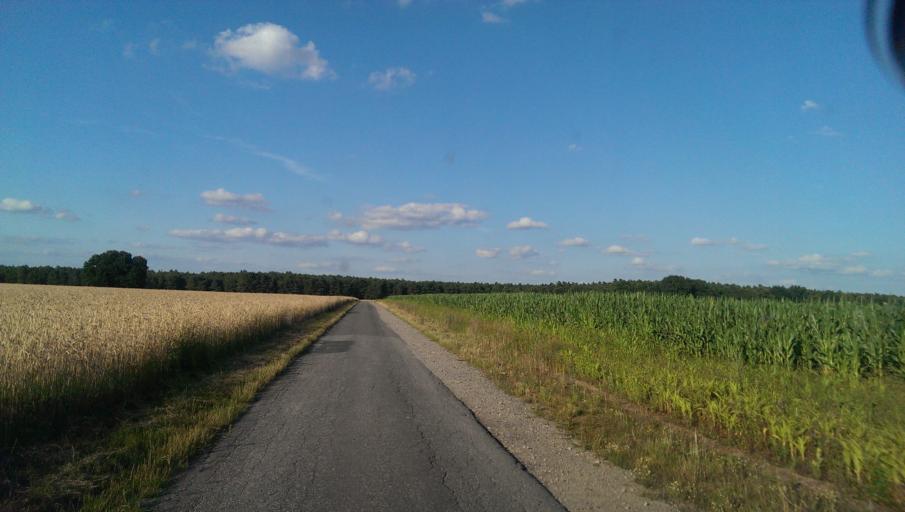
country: DE
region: Brandenburg
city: Treuenbrietzen
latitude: 52.0271
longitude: 12.8496
